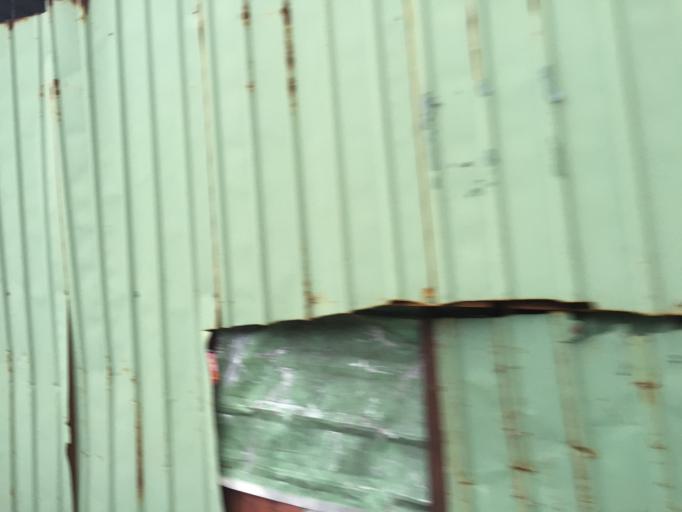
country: TW
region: Taiwan
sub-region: Yilan
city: Yilan
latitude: 24.7798
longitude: 121.7405
